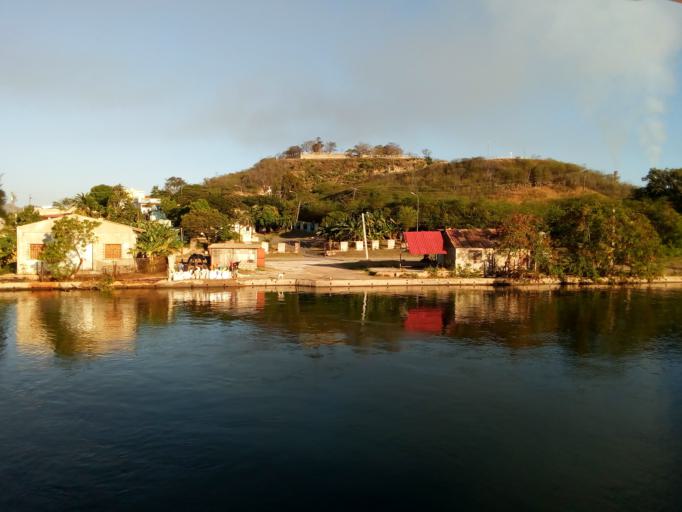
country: CU
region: Santiago de Cuba
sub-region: Municipio de Santiago de Cuba
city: Santiago de Cuba
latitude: 19.9842
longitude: -75.8701
